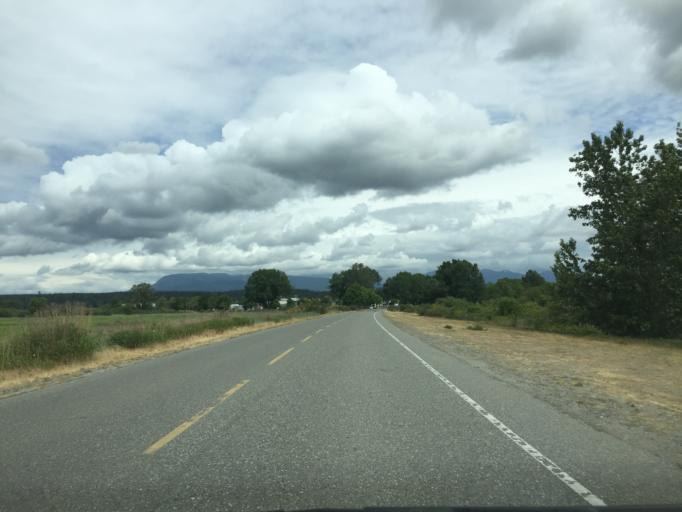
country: CA
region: British Columbia
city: Richmond
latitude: 49.2125
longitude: -123.2024
